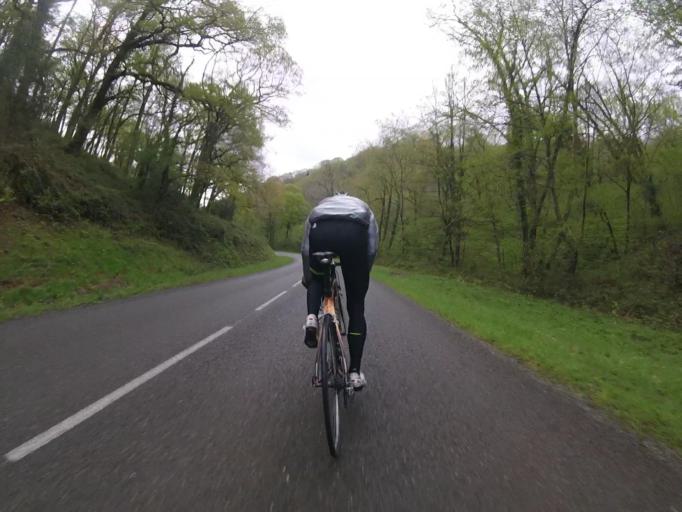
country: FR
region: Aquitaine
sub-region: Departement des Pyrenees-Atlantiques
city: Sare
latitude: 43.2839
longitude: -1.6164
